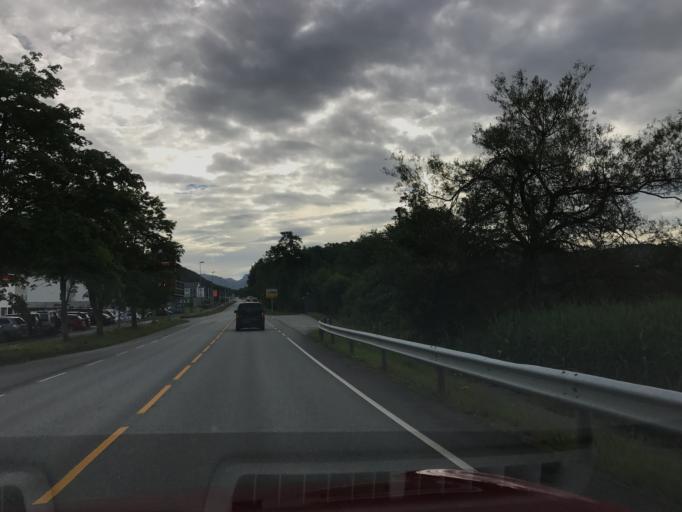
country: NO
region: Rogaland
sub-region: Strand
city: Tau
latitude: 59.0649
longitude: 5.9144
